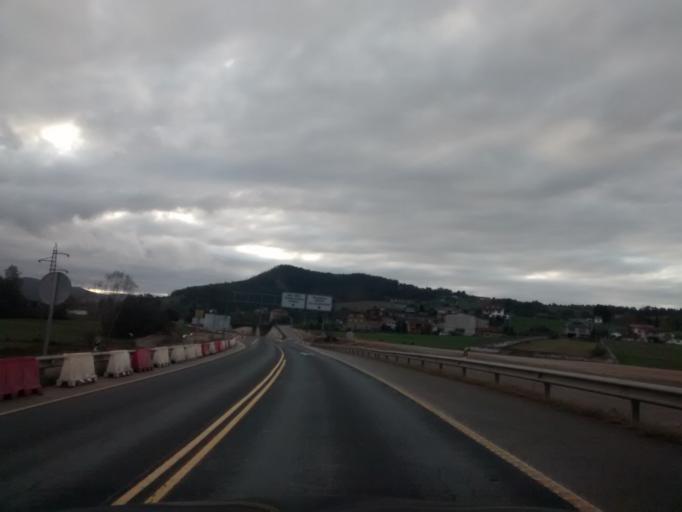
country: ES
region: Cantabria
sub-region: Provincia de Cantabria
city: Santa Maria de Cayon
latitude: 43.3315
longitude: -3.8456
